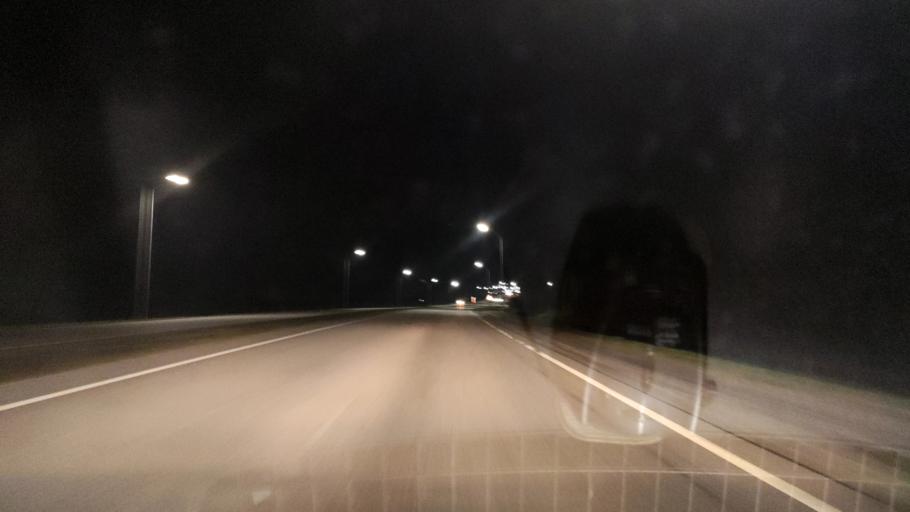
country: RU
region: Belgorod
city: Staryy Oskol
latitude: 51.3784
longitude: 37.8532
